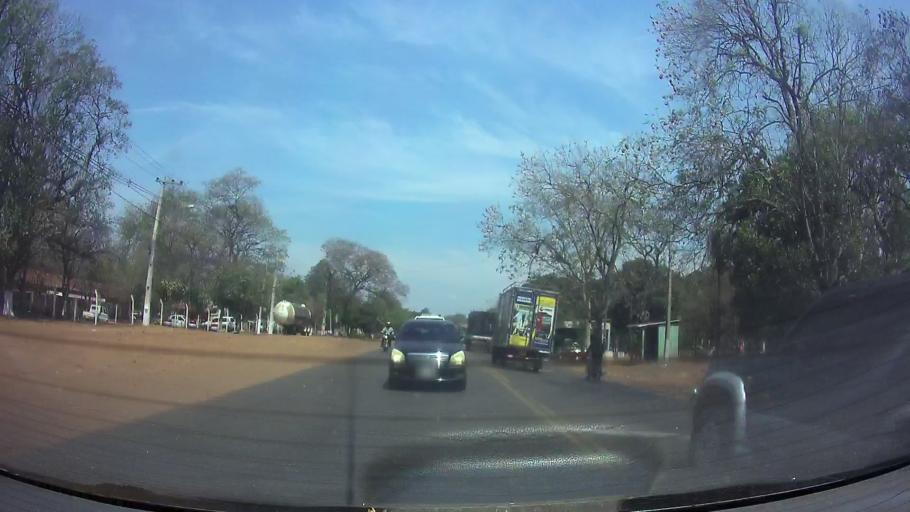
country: PY
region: Central
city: Capiata
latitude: -25.4020
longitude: -57.4639
